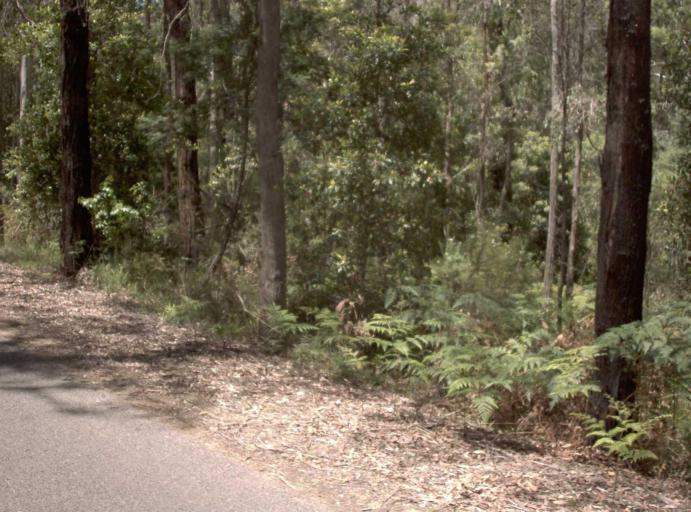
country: AU
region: New South Wales
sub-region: Bombala
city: Bombala
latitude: -37.4448
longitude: 148.9460
